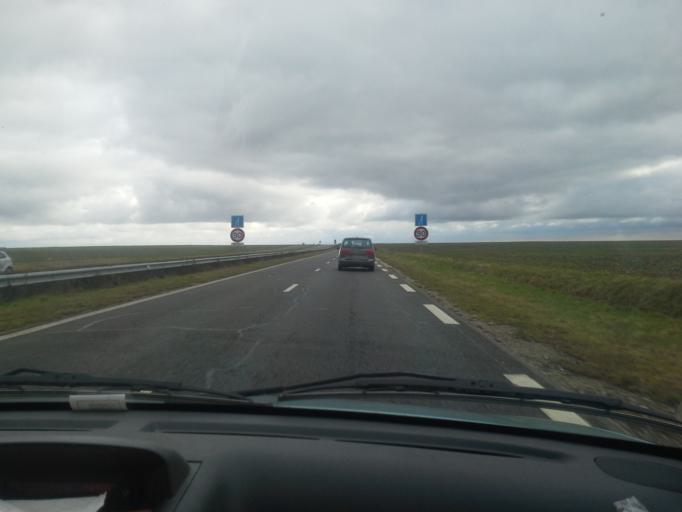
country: FR
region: Centre
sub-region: Departement du Loir-et-Cher
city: Herbault
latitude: 47.7159
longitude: 1.1585
